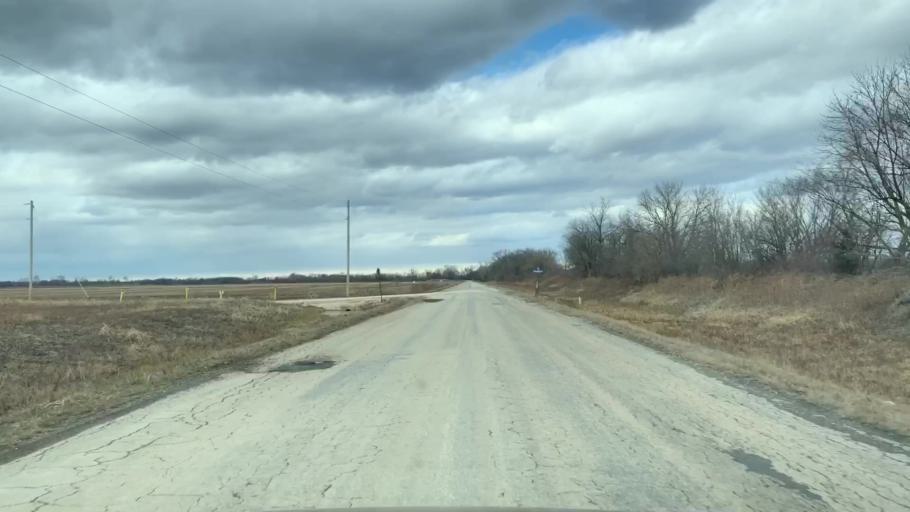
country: US
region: Kansas
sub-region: Allen County
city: Humboldt
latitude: 37.7907
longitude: -95.4706
